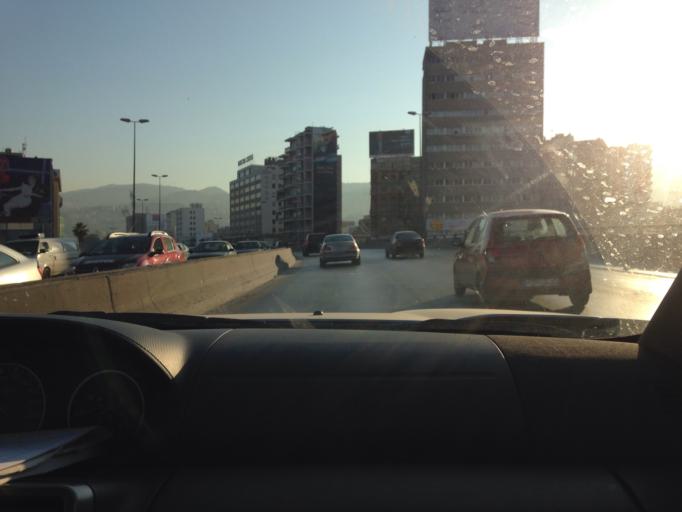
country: LB
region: Mont-Liban
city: Jdaidet el Matn
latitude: 33.8938
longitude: 35.5502
